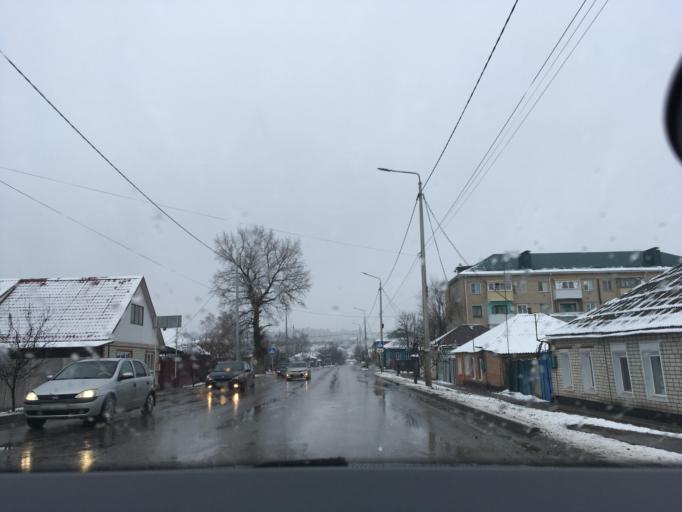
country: RU
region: Belgorod
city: Valuyki
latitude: 50.2048
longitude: 38.1060
